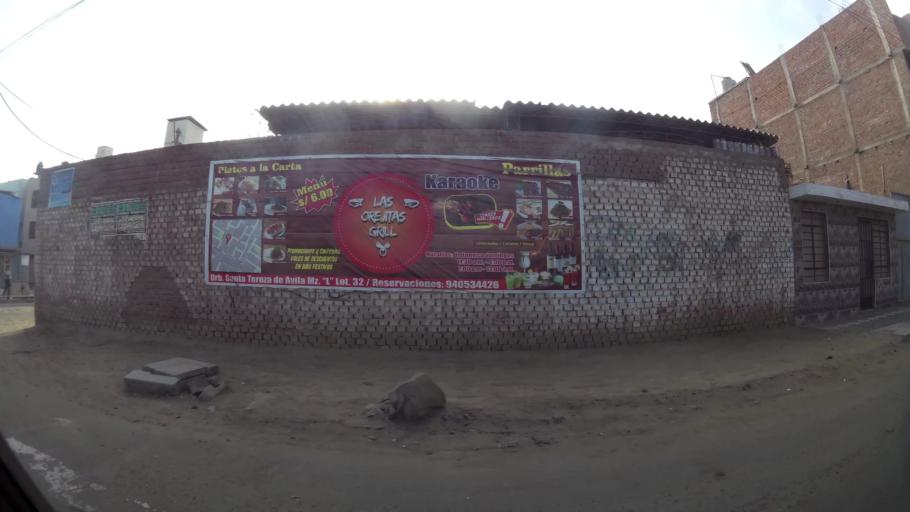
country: PE
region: La Libertad
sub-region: Provincia de Trujillo
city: El Porvenir
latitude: -8.0917
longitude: -79.0139
